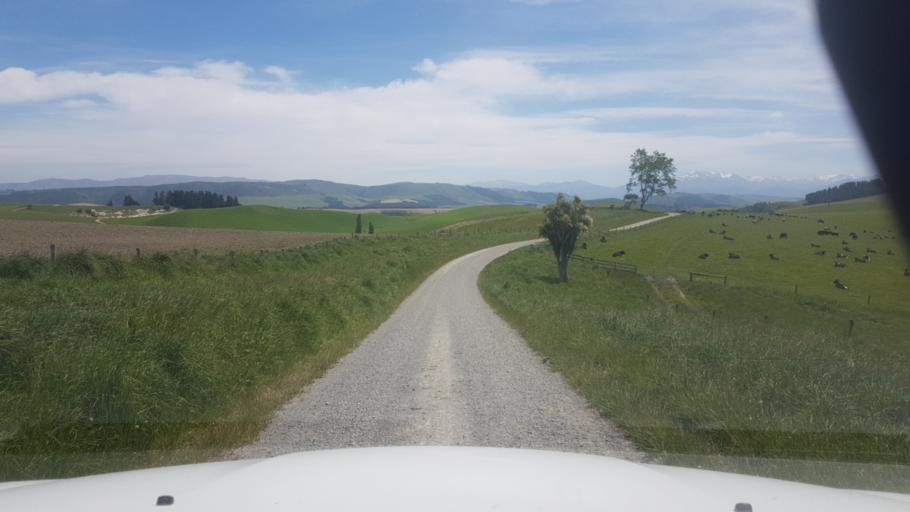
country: NZ
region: Canterbury
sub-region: Timaru District
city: Pleasant Point
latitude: -44.1306
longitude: 171.0173
